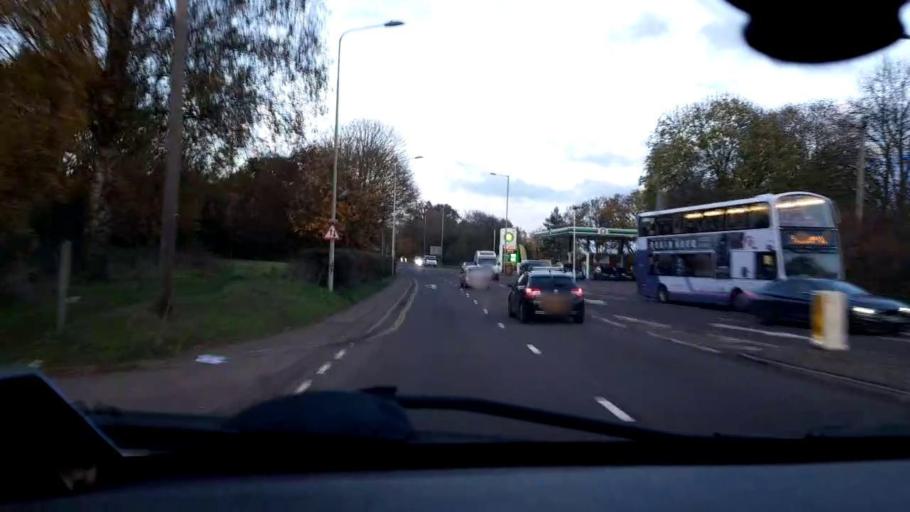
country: GB
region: England
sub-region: Norfolk
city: Thorpe Hamlet
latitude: 52.6124
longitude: 1.3069
